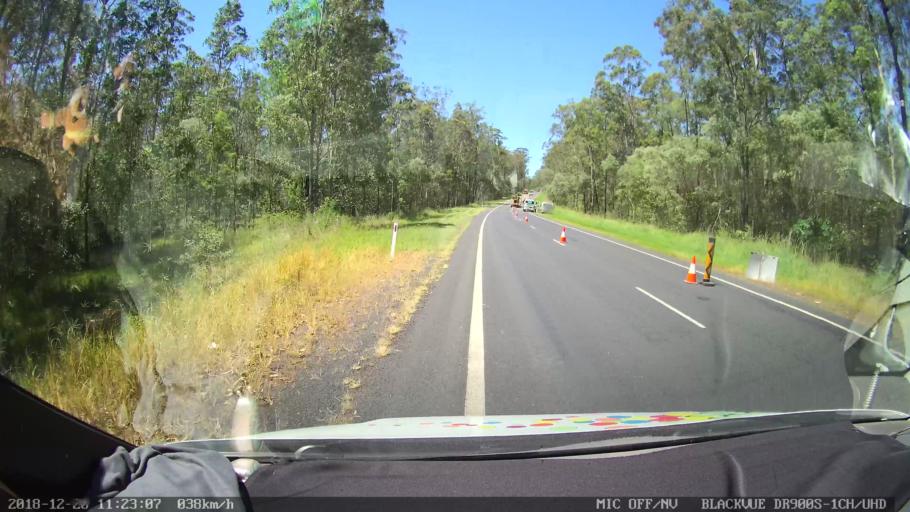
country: AU
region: New South Wales
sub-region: Richmond Valley
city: Casino
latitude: -29.0639
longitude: 153.0047
